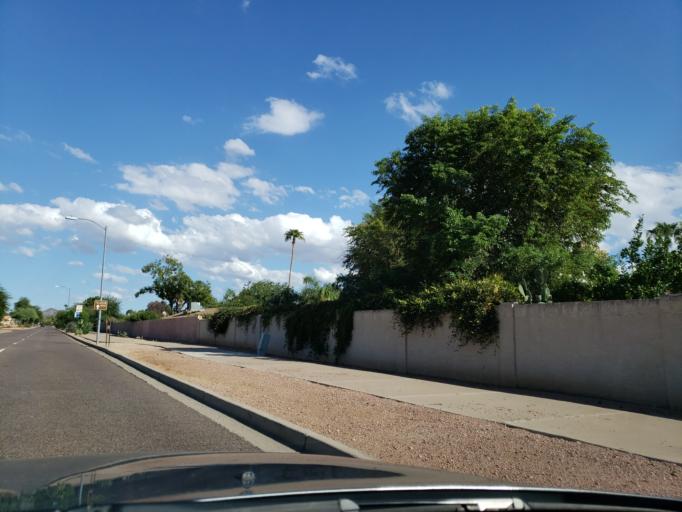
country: US
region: Arizona
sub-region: Maricopa County
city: Scottsdale
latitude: 33.5860
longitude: -111.8484
